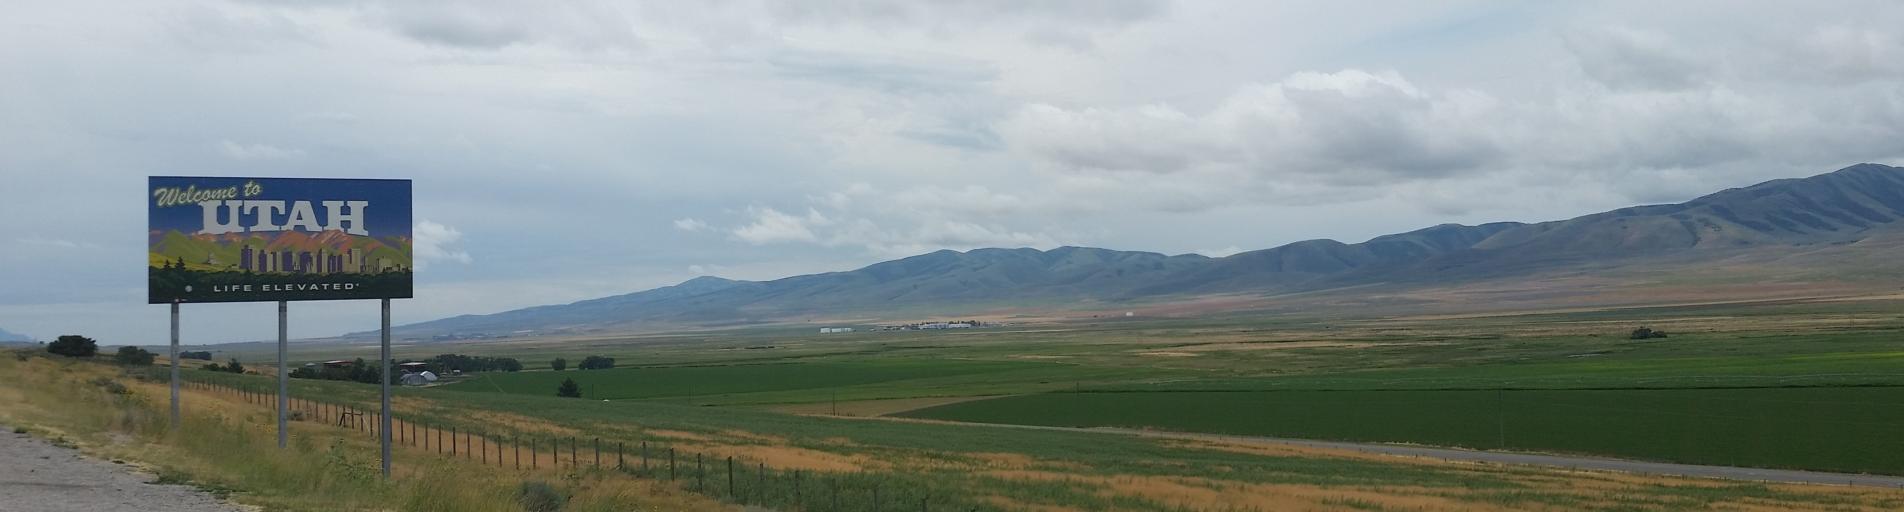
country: US
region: Idaho
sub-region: Oneida County
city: Malad City
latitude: 42.0015
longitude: -112.1992
